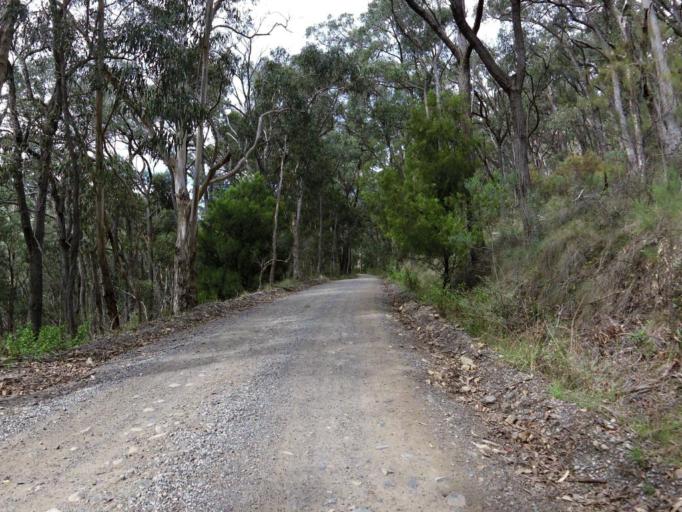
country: AU
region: Victoria
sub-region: Knox
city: The Basin
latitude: -37.8579
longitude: 145.3380
